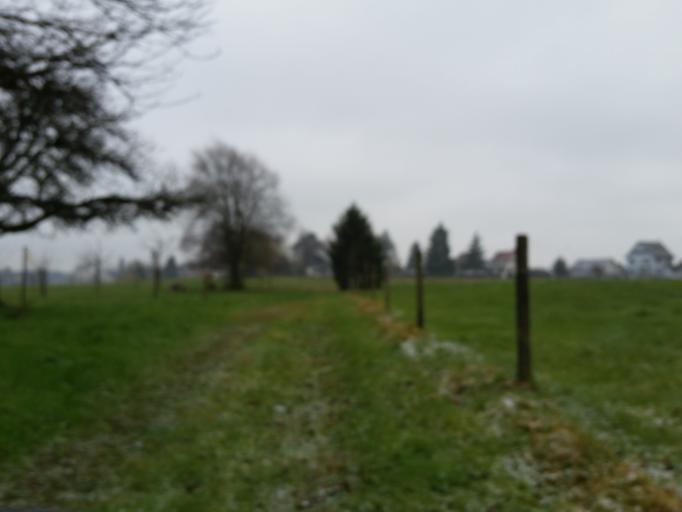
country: CH
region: Thurgau
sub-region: Arbon District
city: Egnach
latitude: 47.5252
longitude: 9.3796
